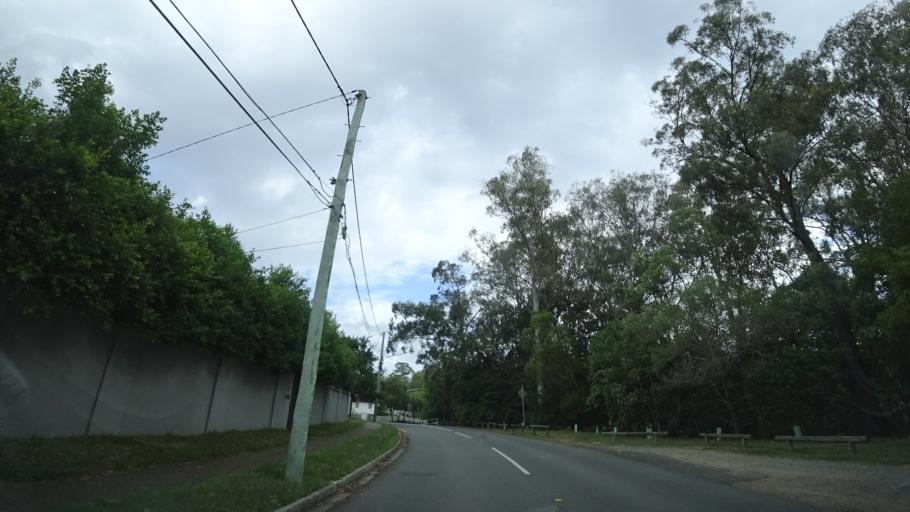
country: AU
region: Queensland
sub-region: Brisbane
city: Toowong
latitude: -27.4590
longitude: 152.9786
